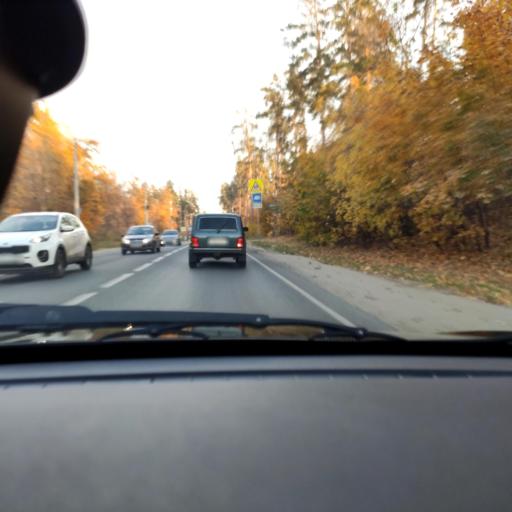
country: RU
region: Samara
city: Tol'yatti
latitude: 53.4927
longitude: 49.2992
